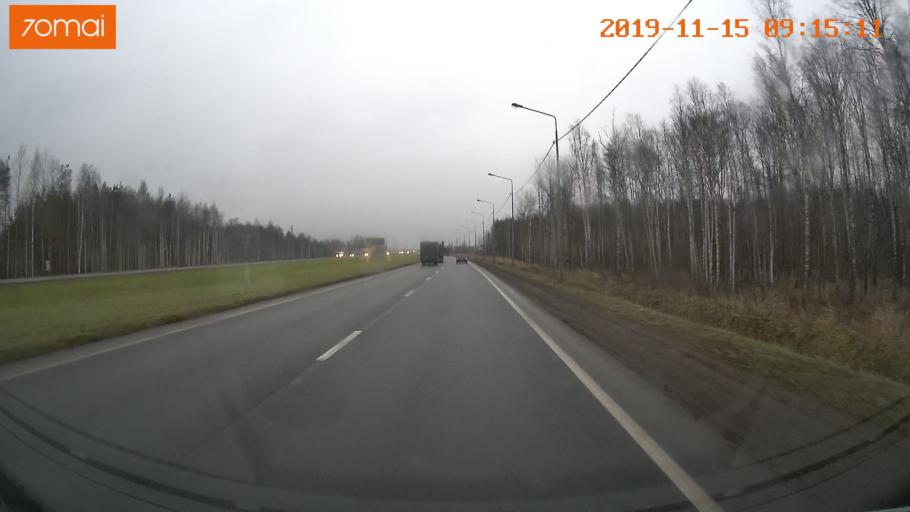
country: RU
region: Vologda
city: Tonshalovo
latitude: 59.2357
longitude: 37.9650
